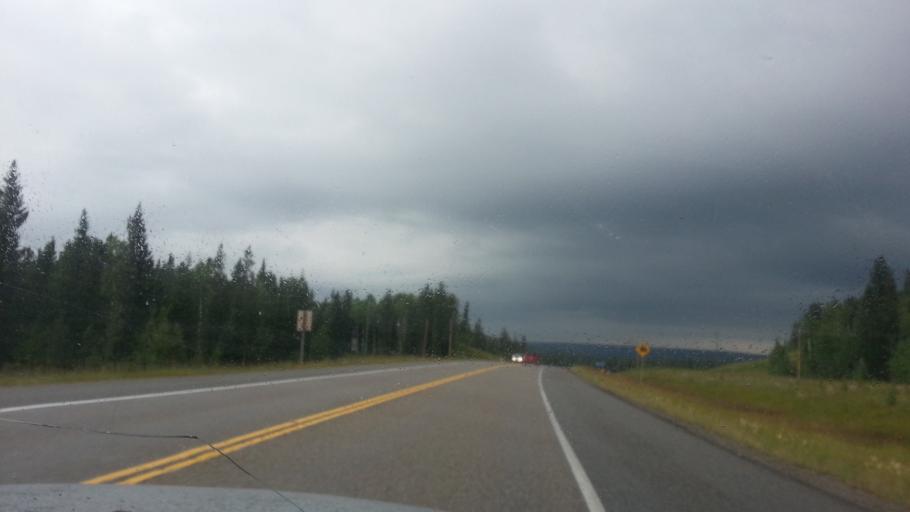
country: CA
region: Alberta
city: Cochrane
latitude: 50.9456
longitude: -114.5605
